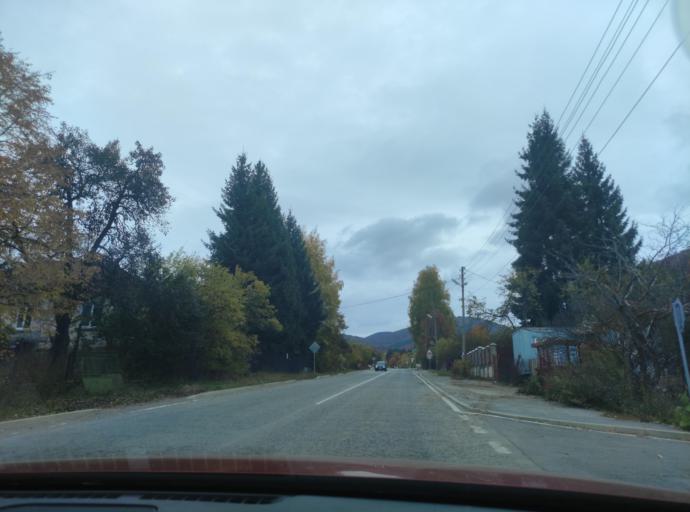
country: BG
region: Sofiya
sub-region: Obshtina Godech
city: Godech
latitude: 43.0949
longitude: 23.0994
